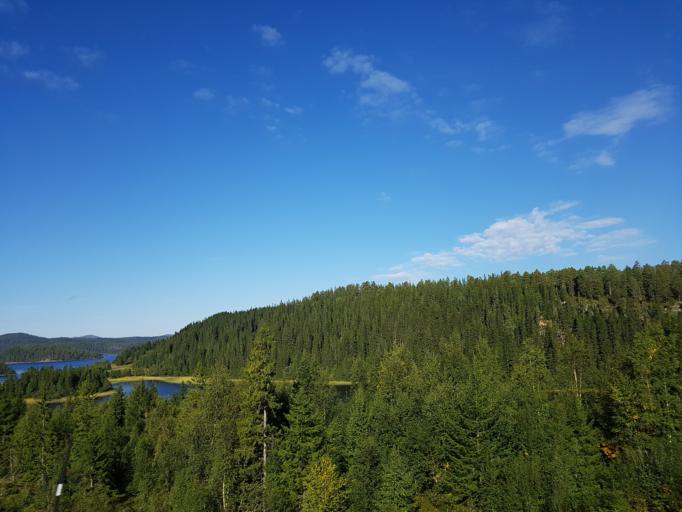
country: NO
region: Sor-Trondelag
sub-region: Trondheim
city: Trondheim
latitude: 63.6057
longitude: 10.2296
